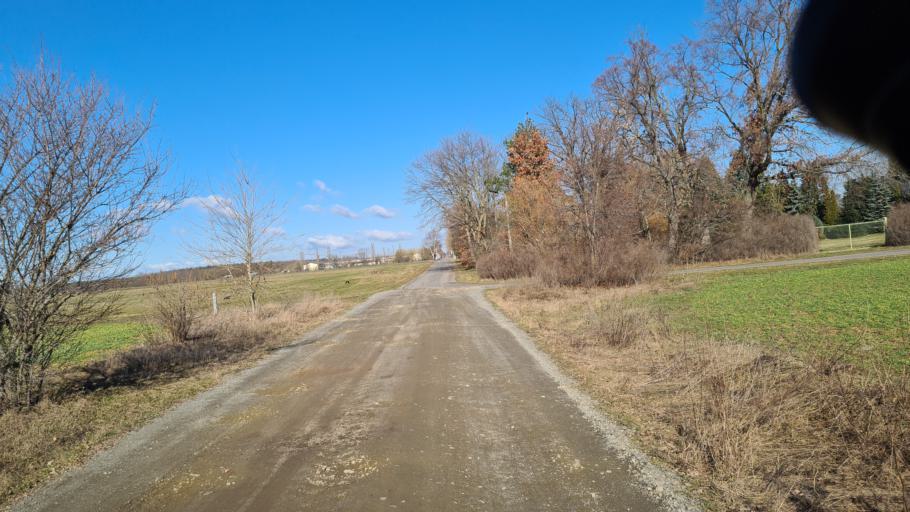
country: DE
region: Brandenburg
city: Falkenberg
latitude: 51.5610
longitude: 13.2239
